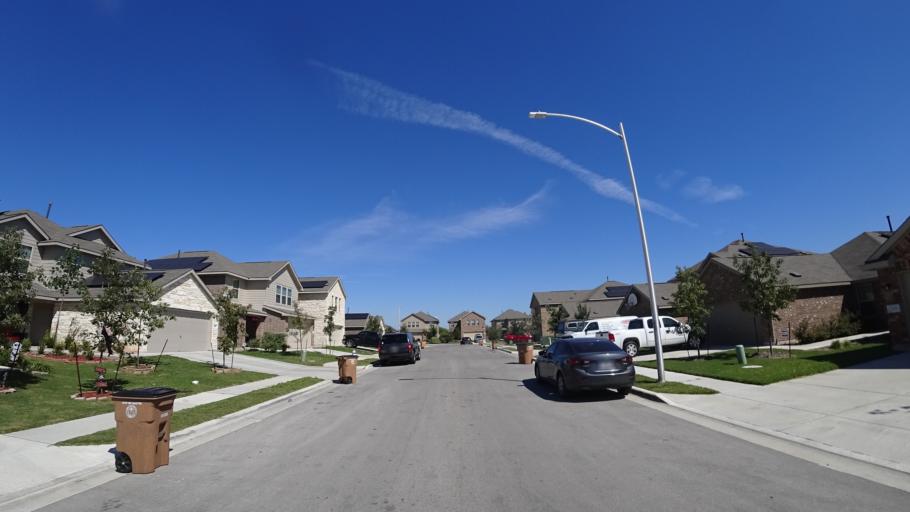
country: US
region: Texas
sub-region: Travis County
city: Austin
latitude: 30.2018
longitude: -97.6967
